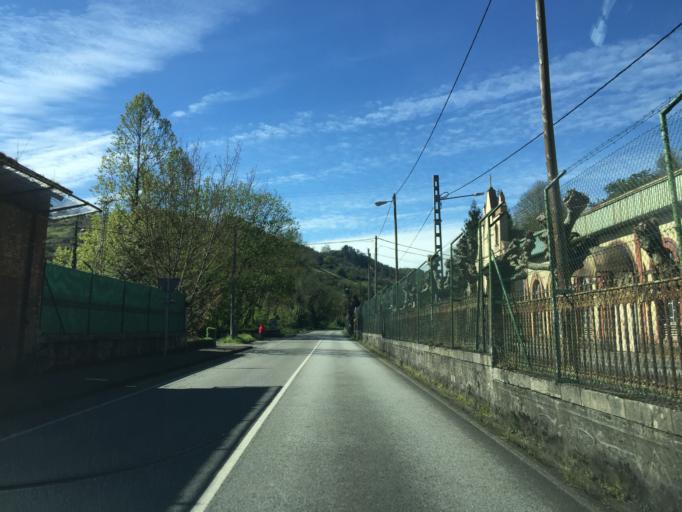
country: ES
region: Asturias
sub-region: Province of Asturias
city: Castandiello
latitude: 43.3497
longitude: -5.9693
